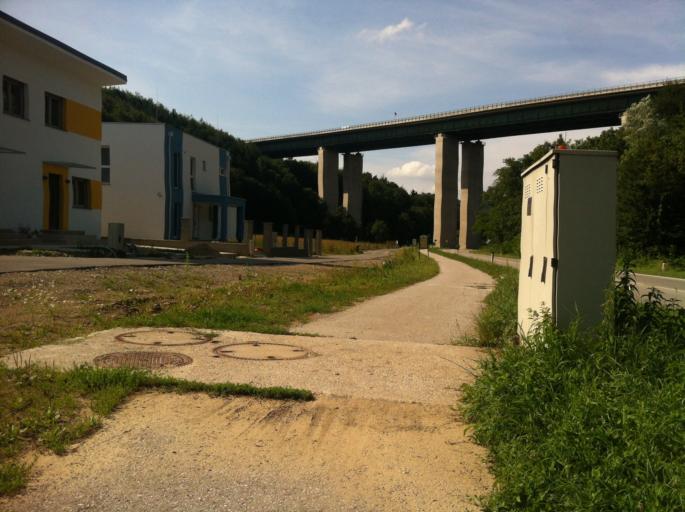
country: AT
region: Lower Austria
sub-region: Politischer Bezirk Wien-Umgebung
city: Wolfsgraben
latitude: 48.1731
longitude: 16.1239
